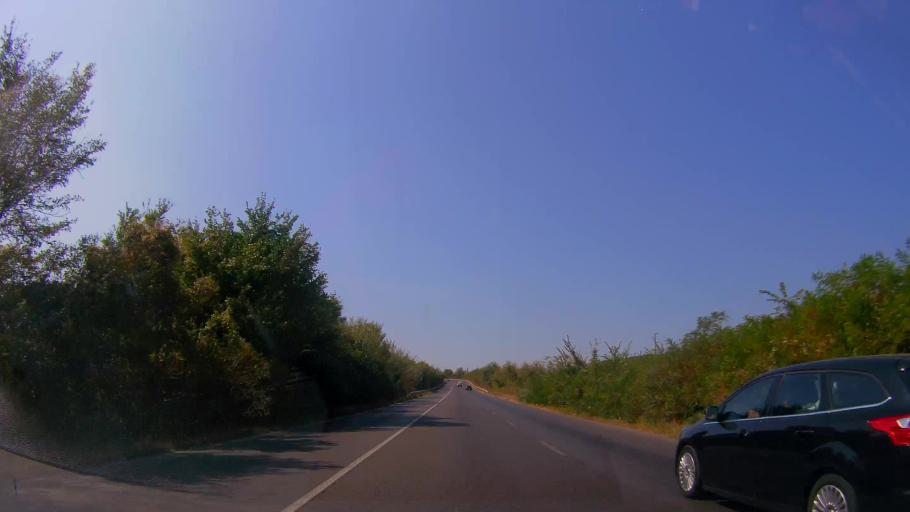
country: BG
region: Ruse
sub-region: Obshtina Vetovo
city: Senovo
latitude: 43.5609
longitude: 26.3831
